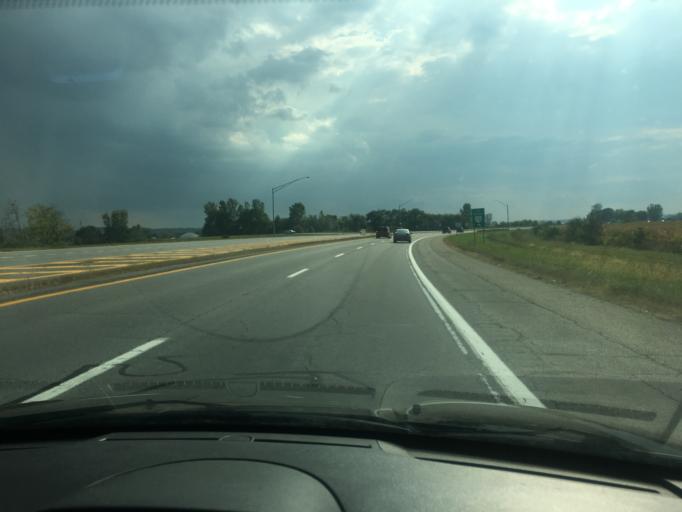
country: US
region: Ohio
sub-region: Clark County
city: Northridge
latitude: 40.0414
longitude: -83.7807
